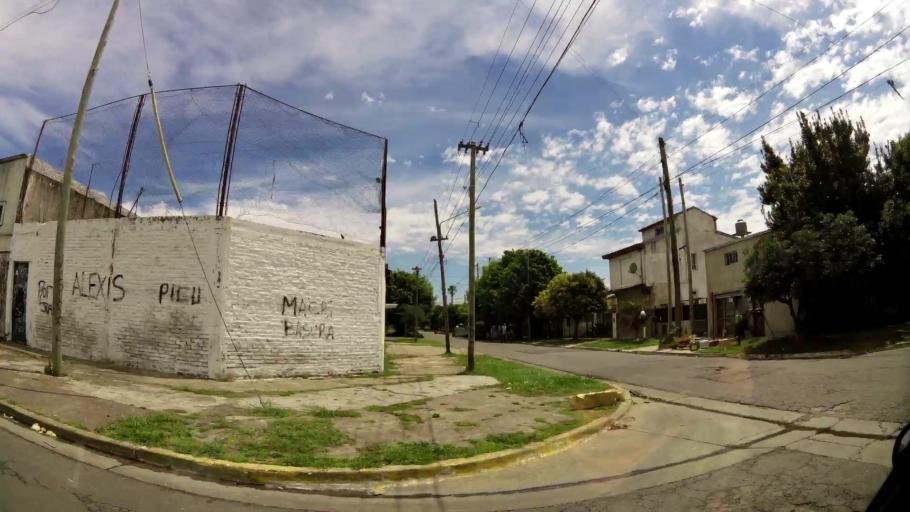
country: AR
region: Buenos Aires
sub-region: Partido de Quilmes
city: Quilmes
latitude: -34.7703
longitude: -58.2384
